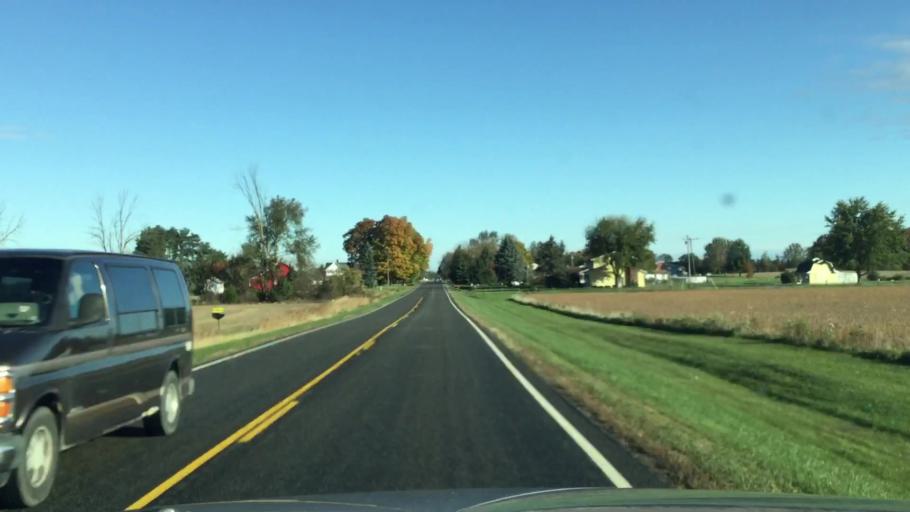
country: US
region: Michigan
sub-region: Shiawassee County
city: Durand
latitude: 42.9031
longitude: -83.9481
